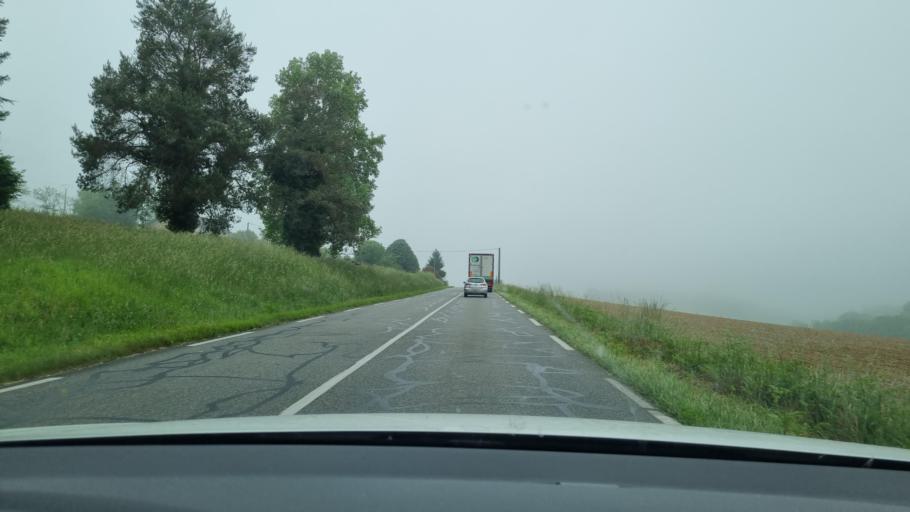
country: FR
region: Aquitaine
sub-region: Departement des Pyrenees-Atlantiques
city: Orthez
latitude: 43.5097
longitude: -0.7311
